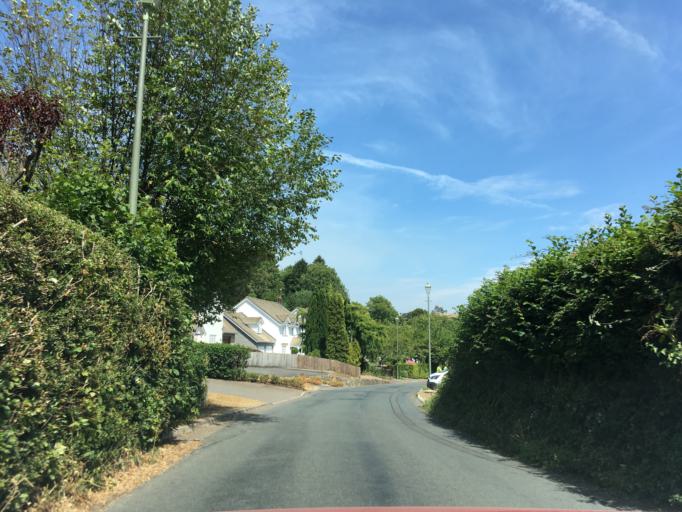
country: GB
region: Wales
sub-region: Caerphilly County Borough
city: Machen
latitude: 51.5789
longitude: -3.1277
